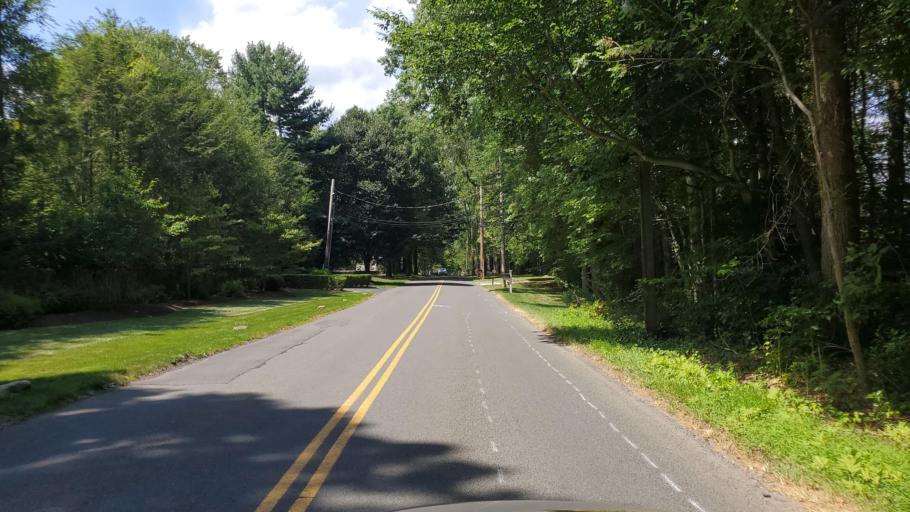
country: US
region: Connecticut
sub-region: Fairfield County
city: Southport
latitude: 41.1664
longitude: -73.2939
